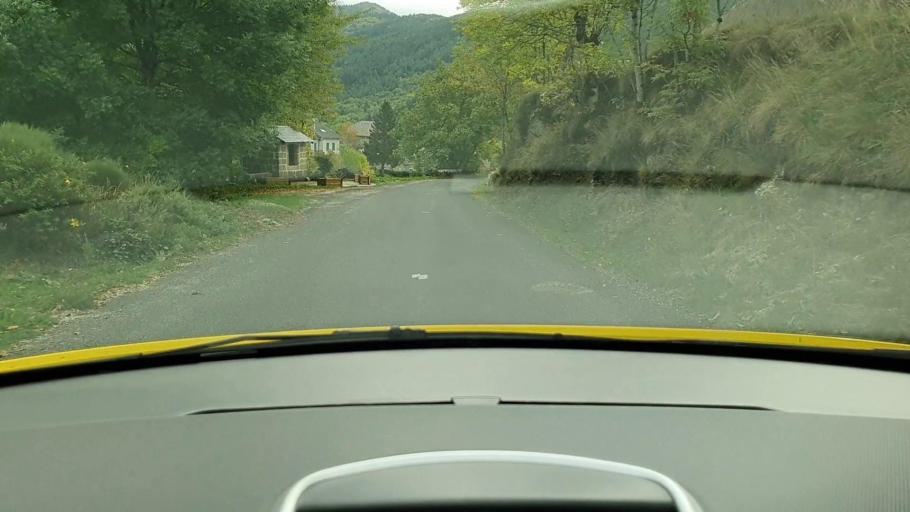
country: FR
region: Languedoc-Roussillon
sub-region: Departement de la Lozere
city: Meyrueis
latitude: 44.0658
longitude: 3.4463
